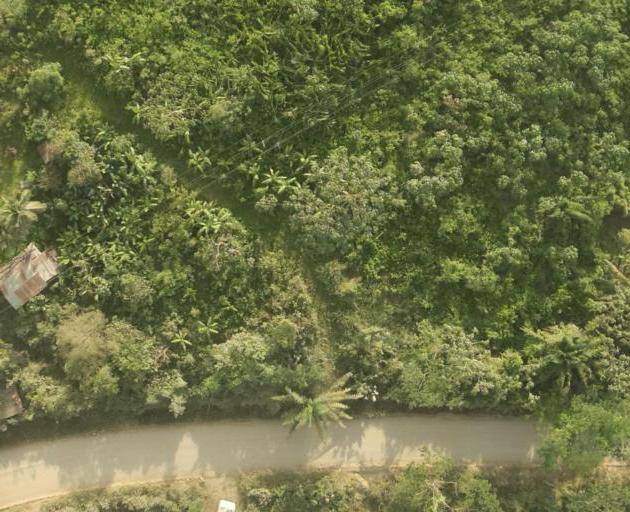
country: BO
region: La Paz
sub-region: Provincia Larecaja
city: Guanay
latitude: -15.7722
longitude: -67.6585
